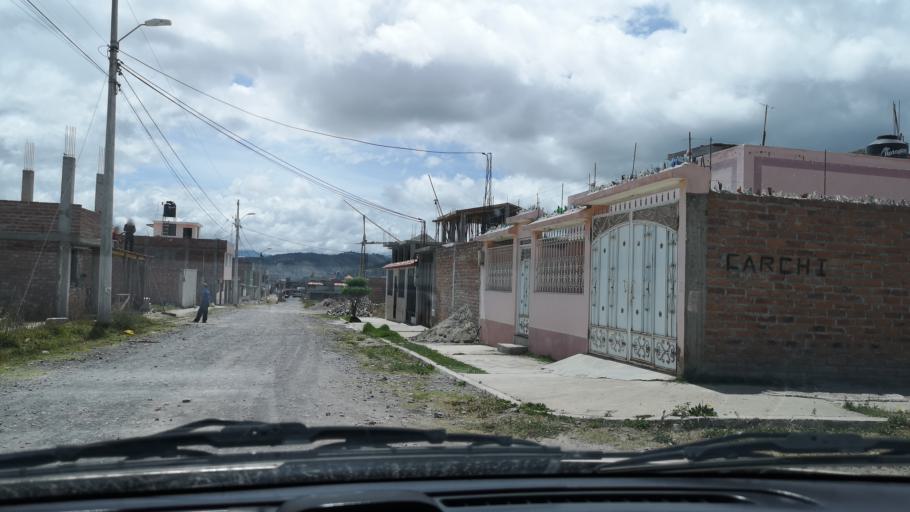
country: EC
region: Chimborazo
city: Riobamba
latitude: -1.6429
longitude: -78.6840
